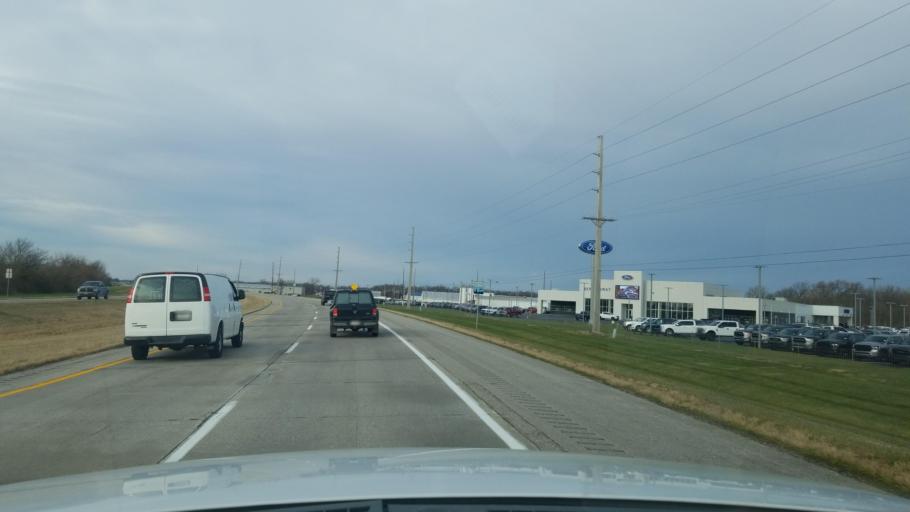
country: US
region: Indiana
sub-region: Posey County
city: Mount Vernon
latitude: 37.9431
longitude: -87.8529
